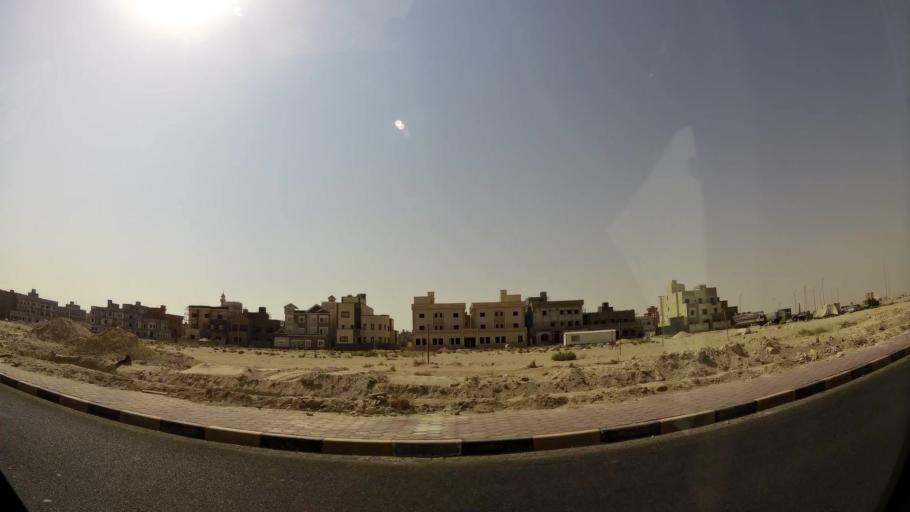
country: KW
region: Al Ahmadi
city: Al Wafrah
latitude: 28.8034
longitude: 48.0470
